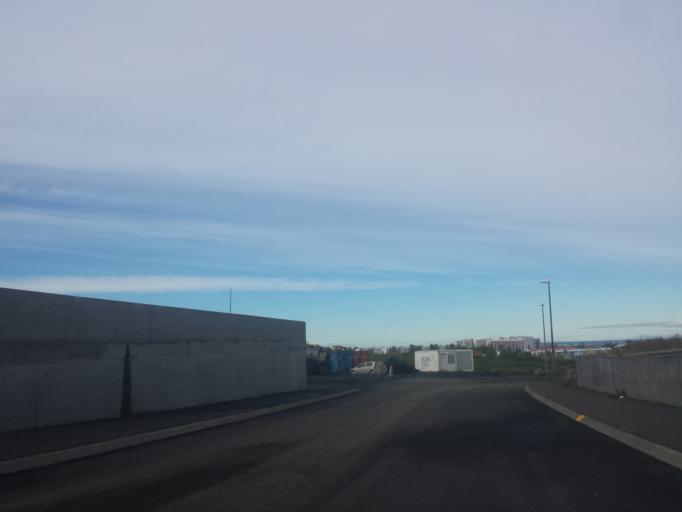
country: IS
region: Capital Region
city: Reykjavik
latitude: 64.0964
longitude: -21.8120
